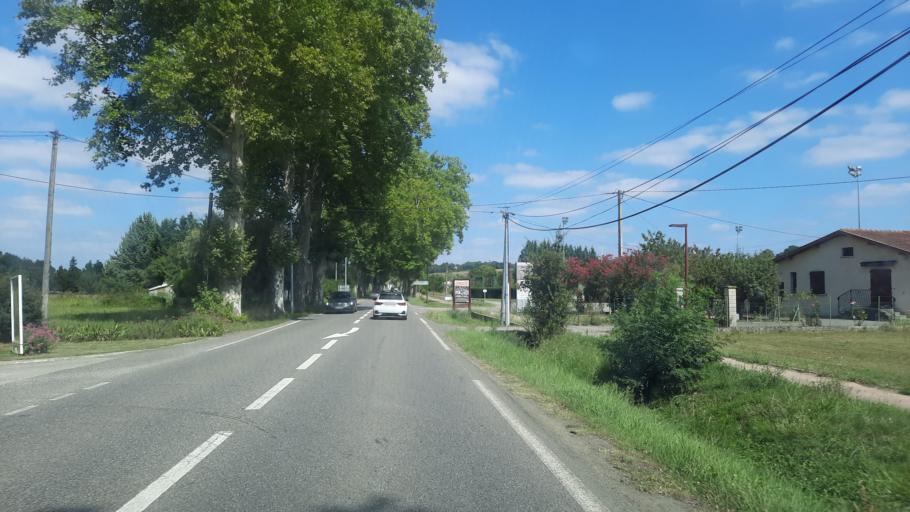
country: FR
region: Midi-Pyrenees
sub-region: Departement du Gers
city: Samatan
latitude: 43.4881
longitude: 0.9364
